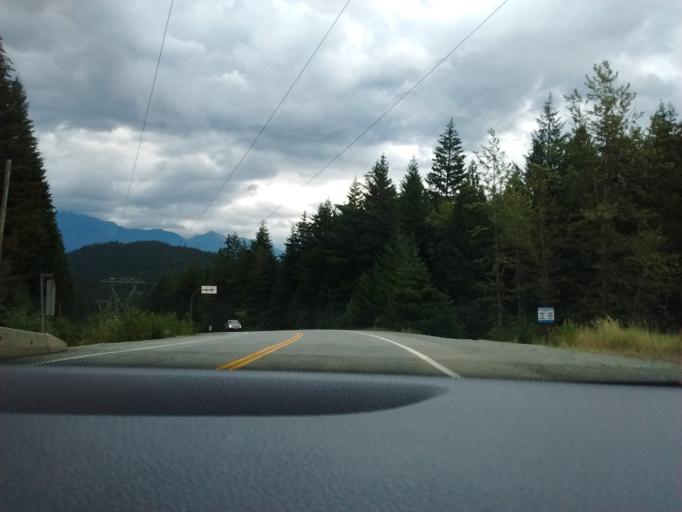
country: CA
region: British Columbia
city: Pemberton
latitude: 50.2935
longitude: -122.8308
